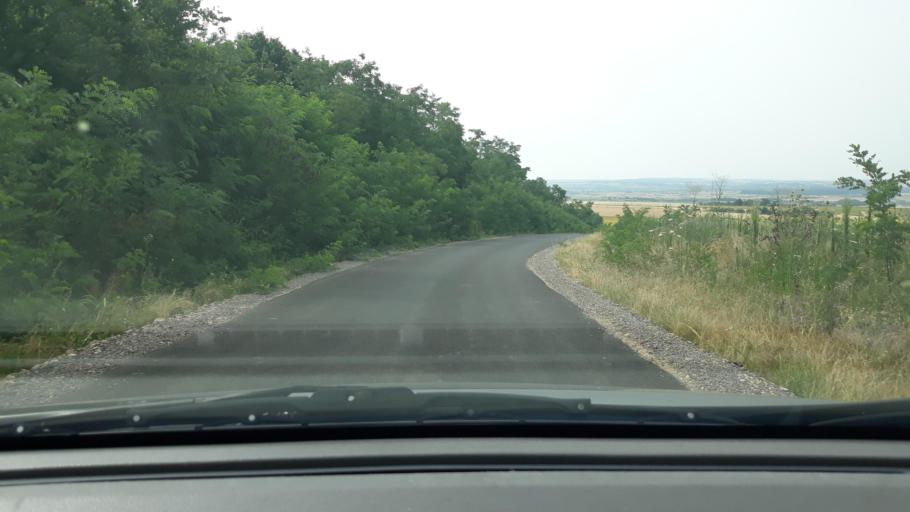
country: RO
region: Bihor
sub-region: Comuna Chislaz
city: Misca
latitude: 47.2619
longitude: 22.2921
